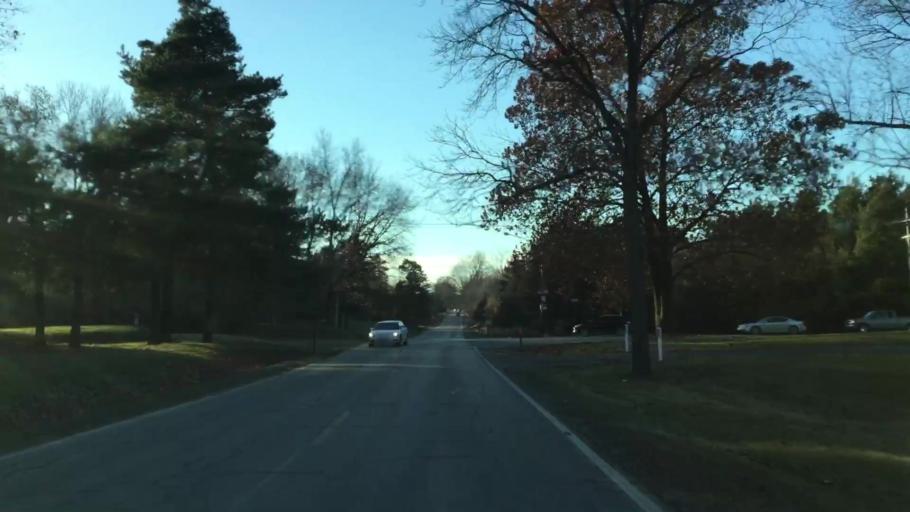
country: US
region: Michigan
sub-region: Genesee County
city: Linden
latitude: 42.7767
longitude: -83.7856
